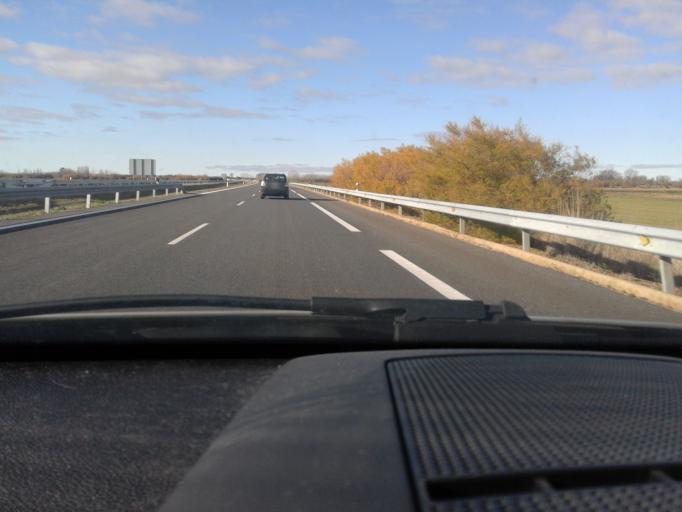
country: ES
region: Castille and Leon
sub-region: Provincia de Palencia
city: Calzada de los Molinos
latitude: 42.3501
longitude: -4.6400
